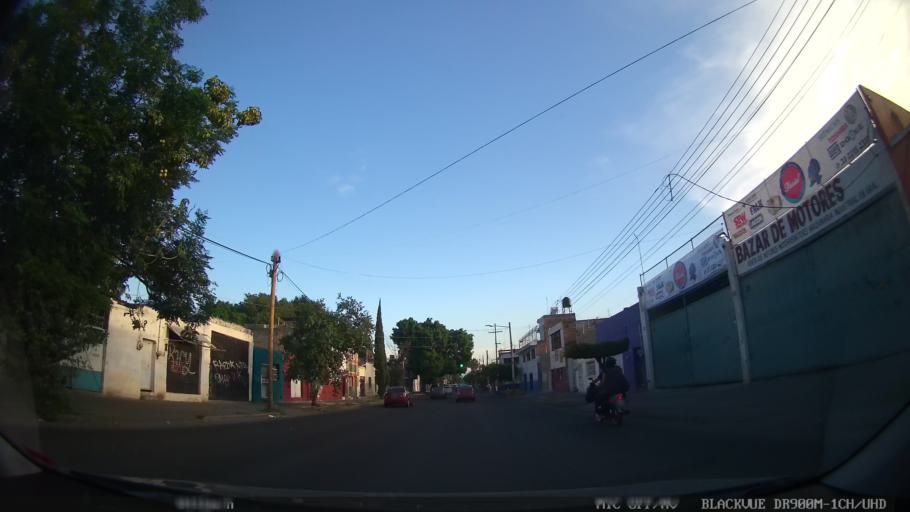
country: MX
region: Jalisco
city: Tlaquepaque
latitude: 20.6667
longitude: -103.3158
